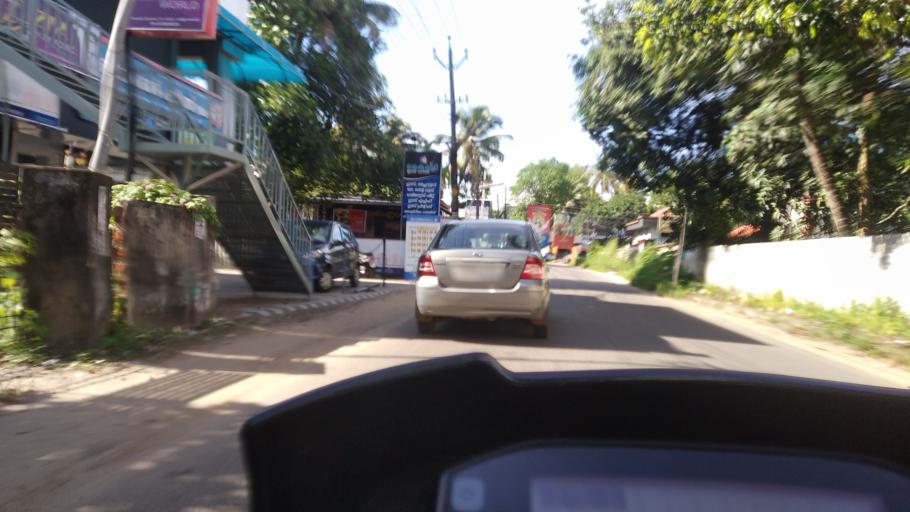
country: IN
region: Kerala
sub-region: Ernakulam
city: Elur
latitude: 10.0501
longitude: 76.2166
